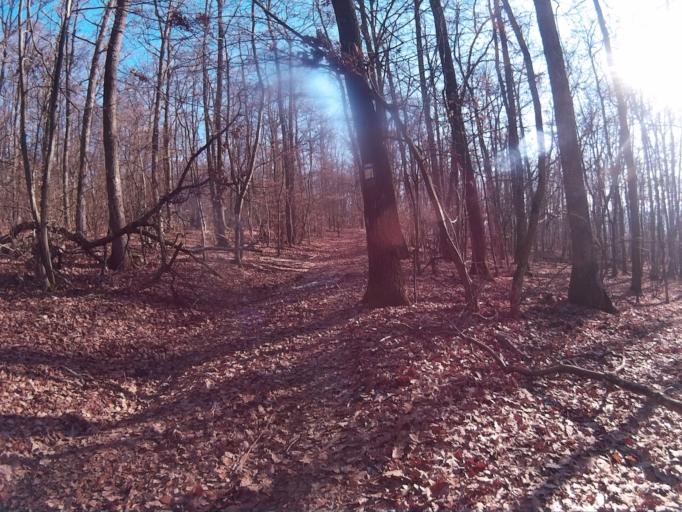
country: HU
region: Borsod-Abauj-Zemplen
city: Rudabanya
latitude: 48.4890
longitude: 20.5765
